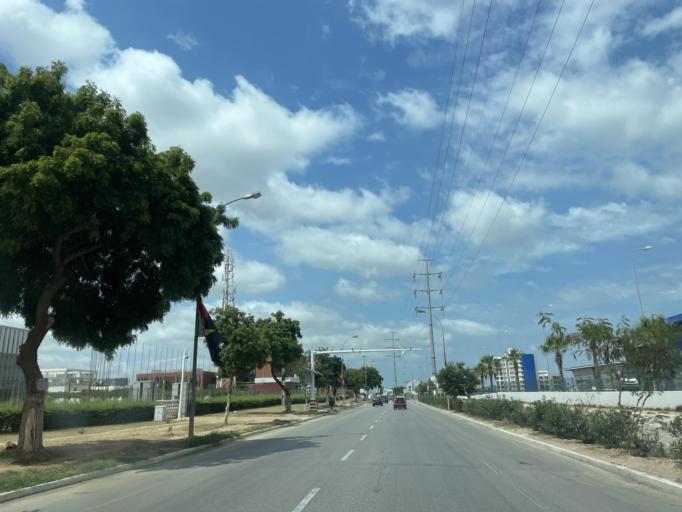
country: AO
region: Luanda
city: Luanda
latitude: -8.9133
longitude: 13.1963
